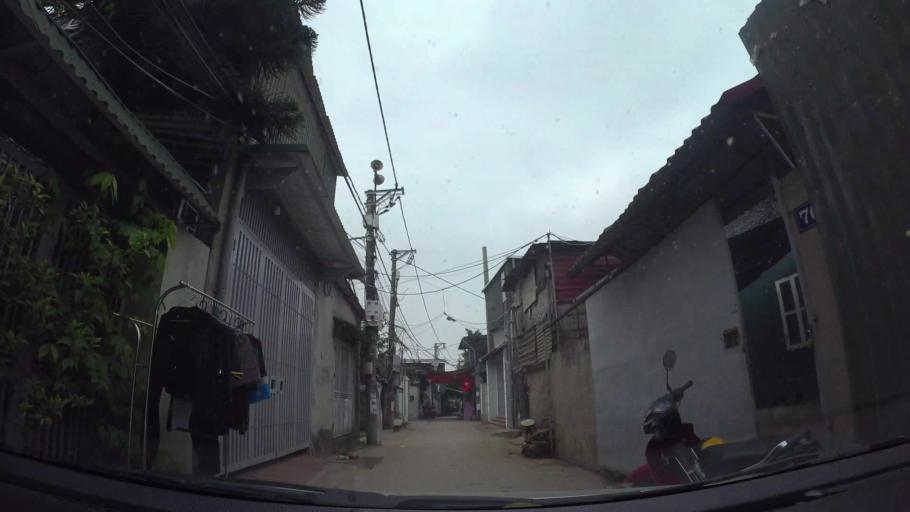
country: VN
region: Ha Noi
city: Tay Ho
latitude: 21.0721
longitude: 105.8284
